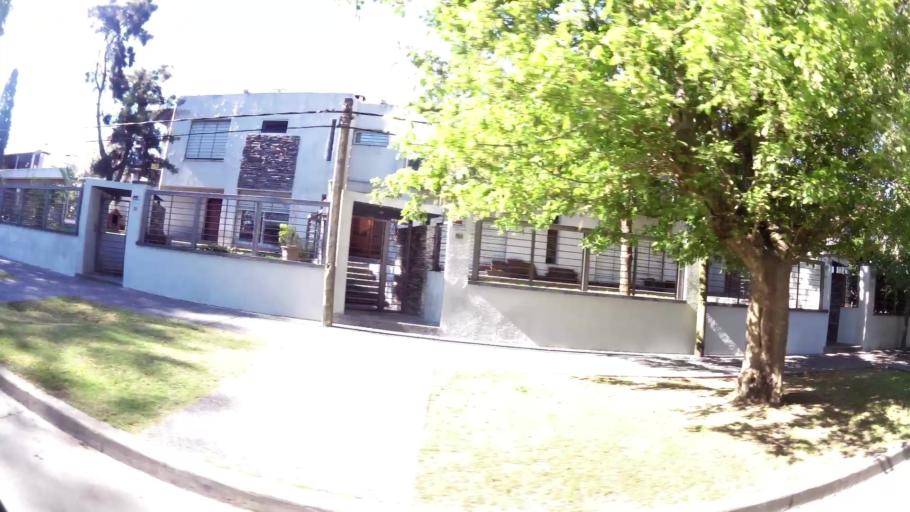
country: UY
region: Canelones
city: Paso de Carrasco
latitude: -34.8907
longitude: -56.0805
